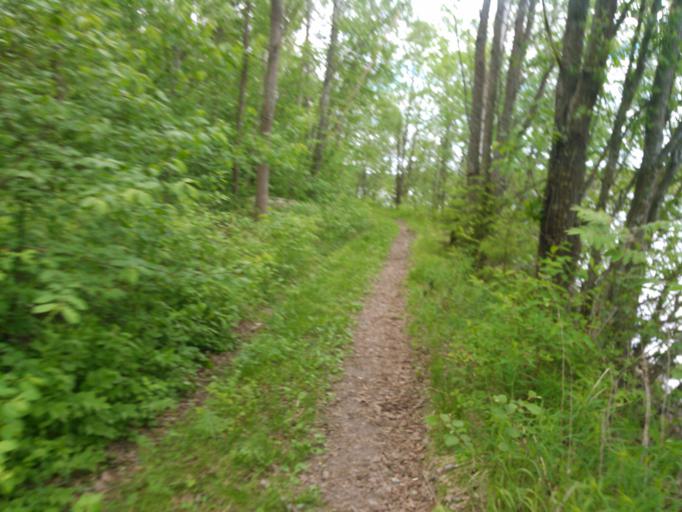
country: SE
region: Vaesterbotten
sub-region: Umea Kommun
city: Roback
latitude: 63.8235
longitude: 20.2035
